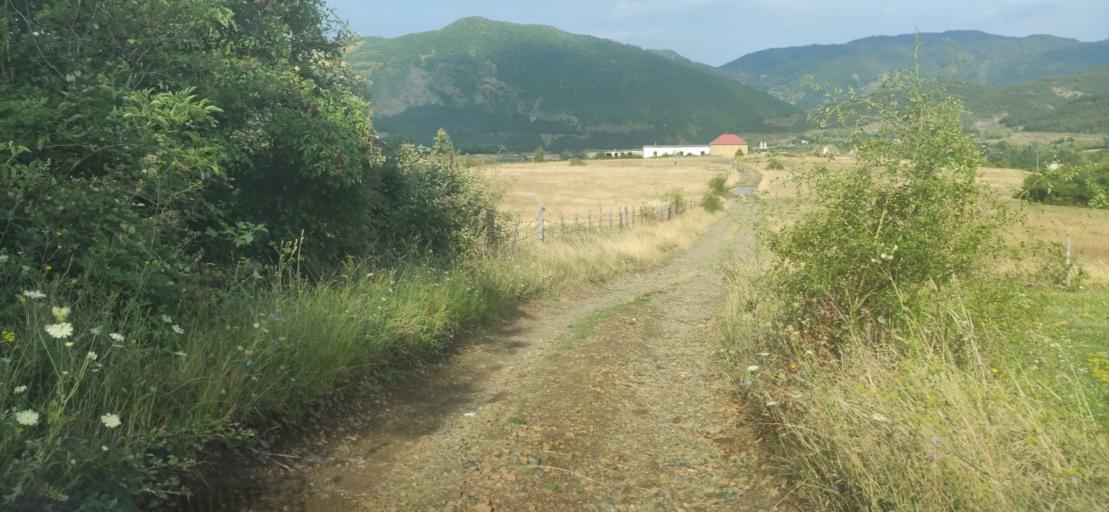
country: AL
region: Shkoder
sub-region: Rrethi i Pukes
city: Iballe
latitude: 42.1870
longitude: 20.0068
